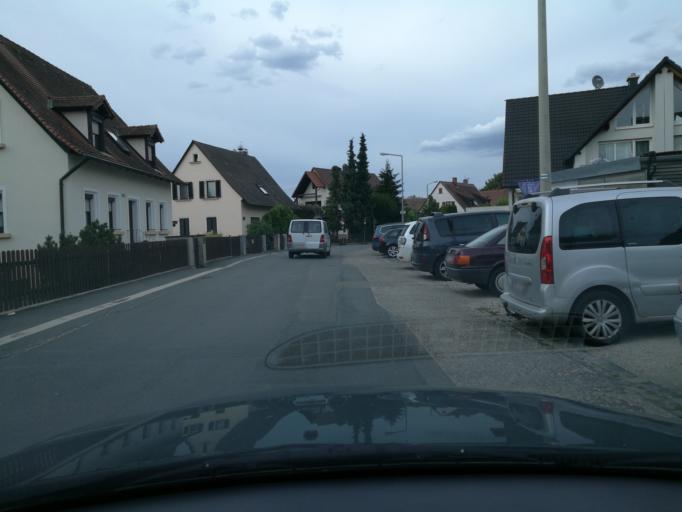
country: DE
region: Bavaria
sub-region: Regierungsbezirk Mittelfranken
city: Wetzendorf
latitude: 49.5099
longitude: 11.0483
